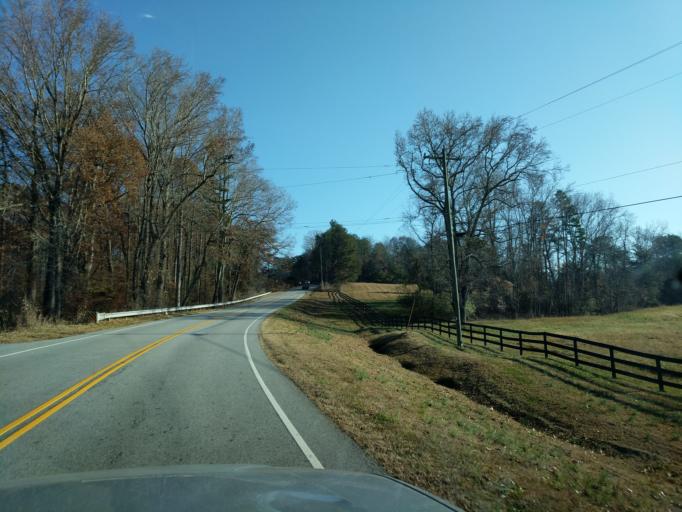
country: US
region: South Carolina
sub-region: Spartanburg County
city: Landrum
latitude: 35.1903
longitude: -82.1428
